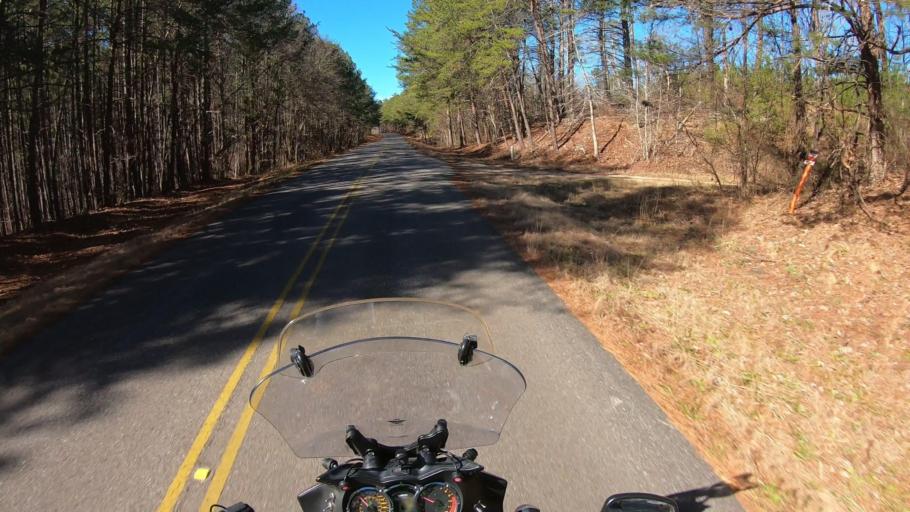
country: US
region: Alabama
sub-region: Clay County
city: Lineville
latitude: 33.4512
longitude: -85.7459
